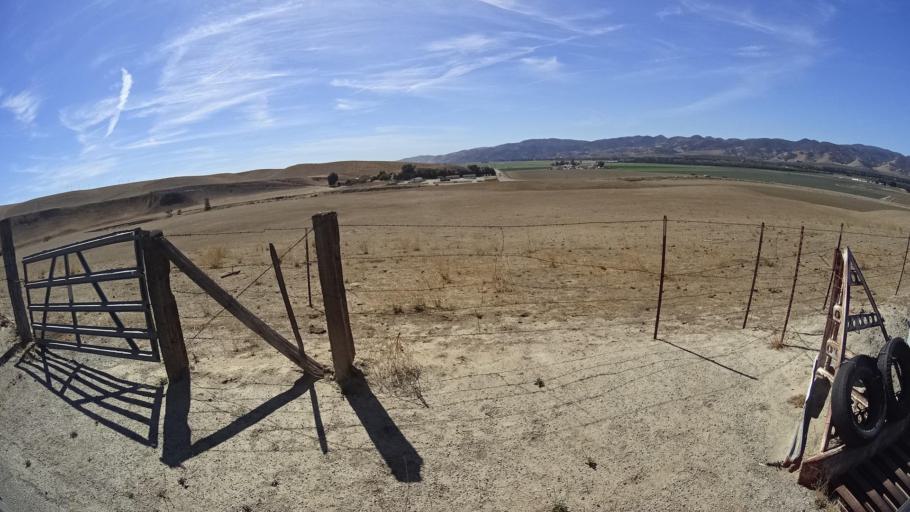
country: US
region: California
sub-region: San Luis Obispo County
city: Lake Nacimiento
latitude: 36.0247
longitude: -120.8854
